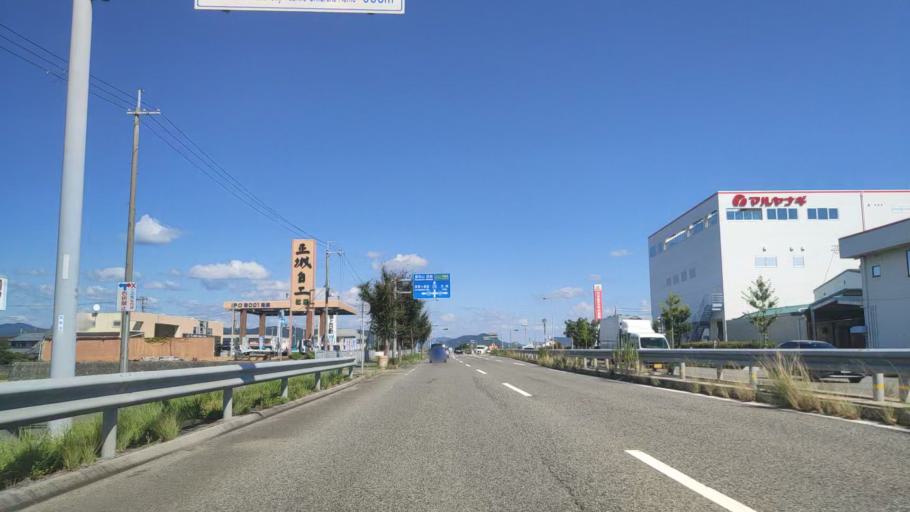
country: JP
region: Hyogo
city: Yashiro
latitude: 34.8948
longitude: 134.9510
